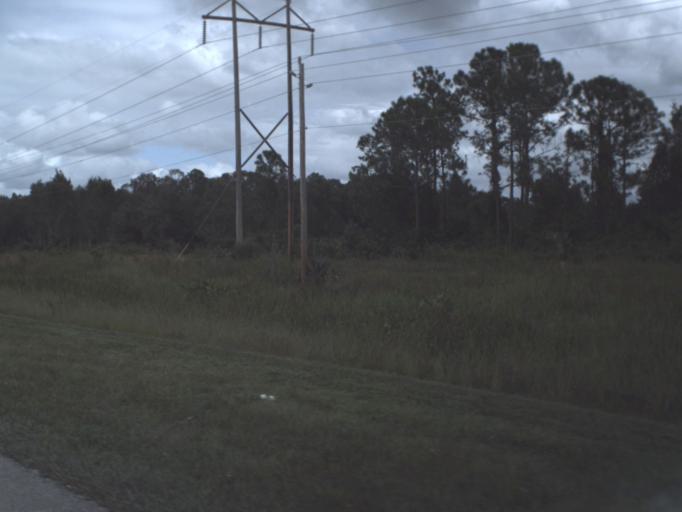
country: US
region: Florida
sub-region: Lee County
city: Gateway
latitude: 26.5717
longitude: -81.6905
